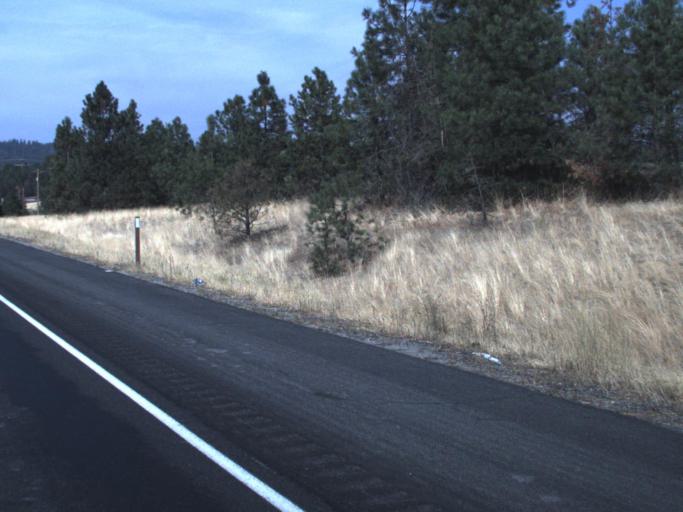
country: US
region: Washington
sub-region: Spokane County
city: Deer Park
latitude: 48.0582
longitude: -117.3443
